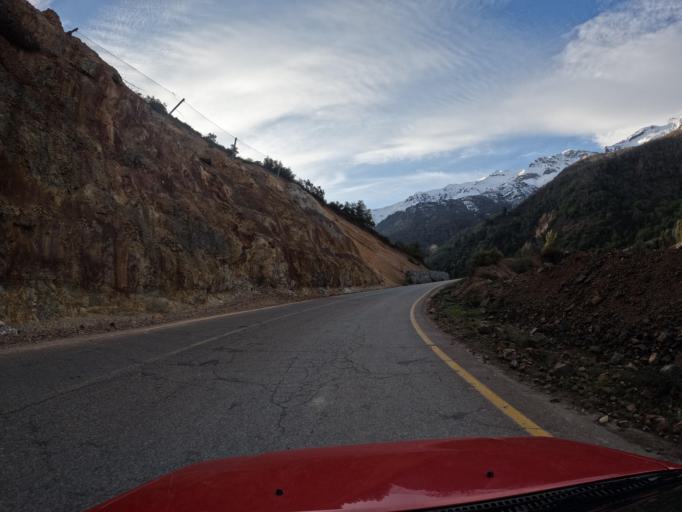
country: CL
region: Maule
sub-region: Provincia de Linares
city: Colbun
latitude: -35.8246
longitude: -70.7657
